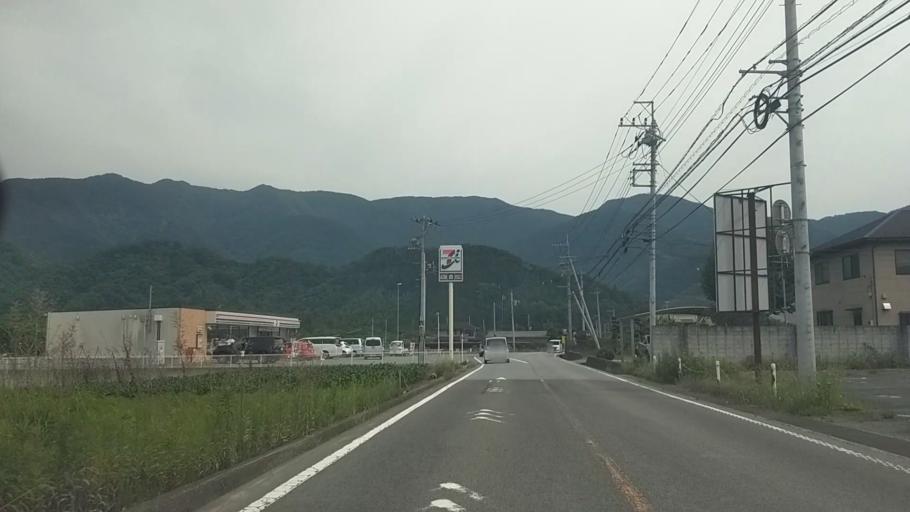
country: JP
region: Yamanashi
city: Isawa
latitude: 35.5823
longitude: 138.5913
